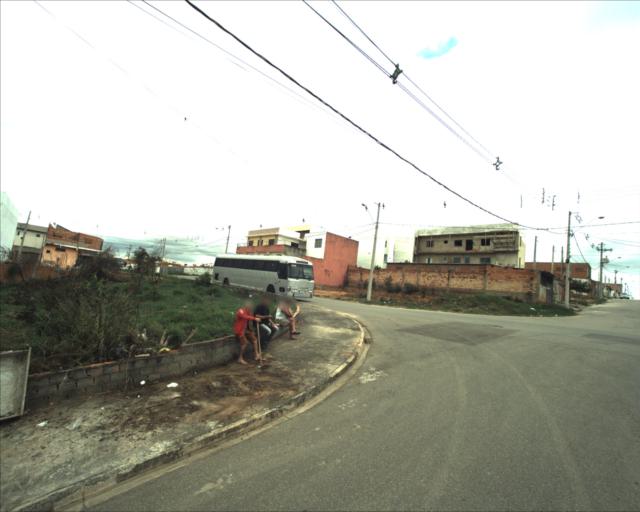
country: BR
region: Sao Paulo
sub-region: Sorocaba
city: Sorocaba
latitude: -23.4379
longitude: -47.4957
